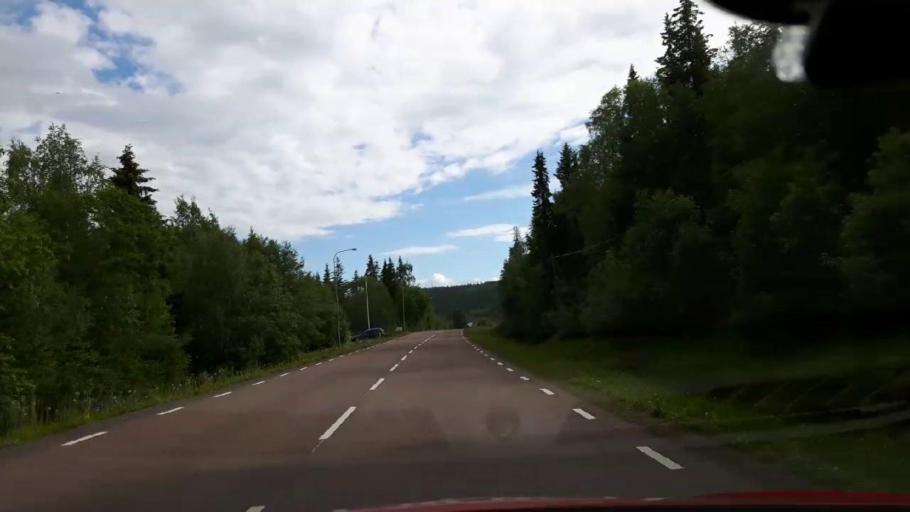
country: SE
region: Jaemtland
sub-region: Krokoms Kommun
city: Valla
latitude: 63.9122
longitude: 14.2163
